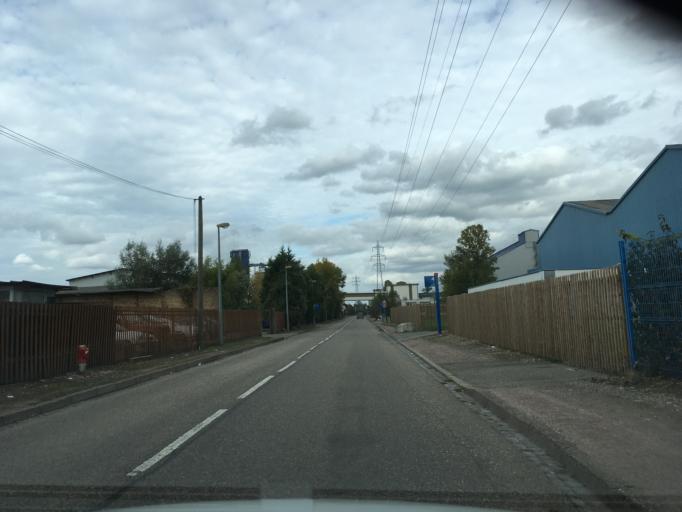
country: DE
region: Baden-Wuerttemberg
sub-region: Freiburg Region
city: Kehl
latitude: 48.5811
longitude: 7.7855
